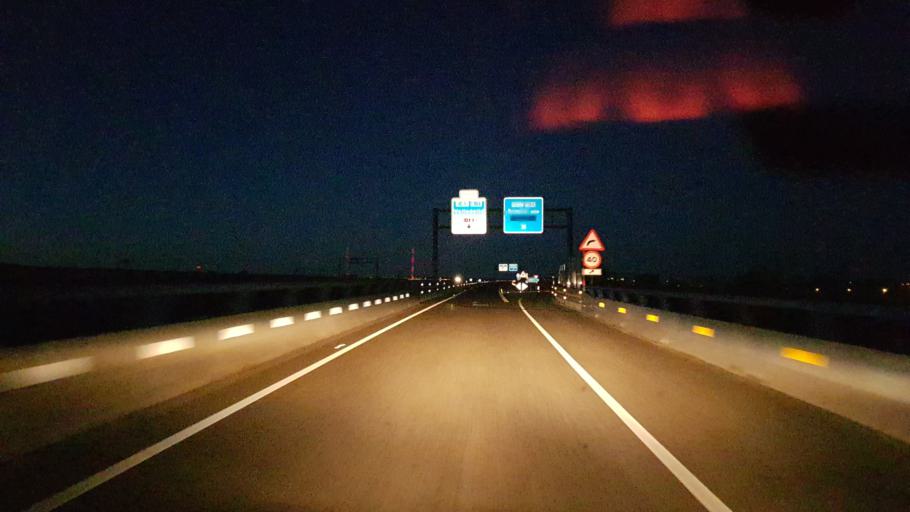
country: ES
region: Castille and Leon
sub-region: Provincia de Zamora
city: Monfarracinos
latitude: 41.5348
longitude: -5.7056
